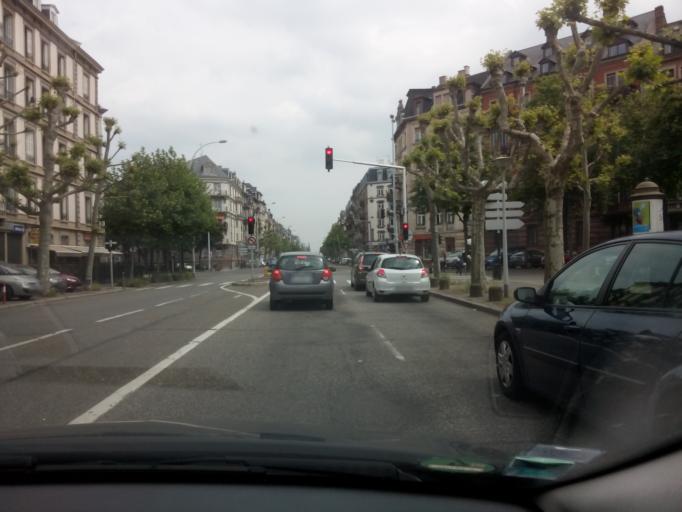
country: FR
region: Alsace
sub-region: Departement du Bas-Rhin
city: Strasbourg
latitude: 48.5912
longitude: 7.7455
